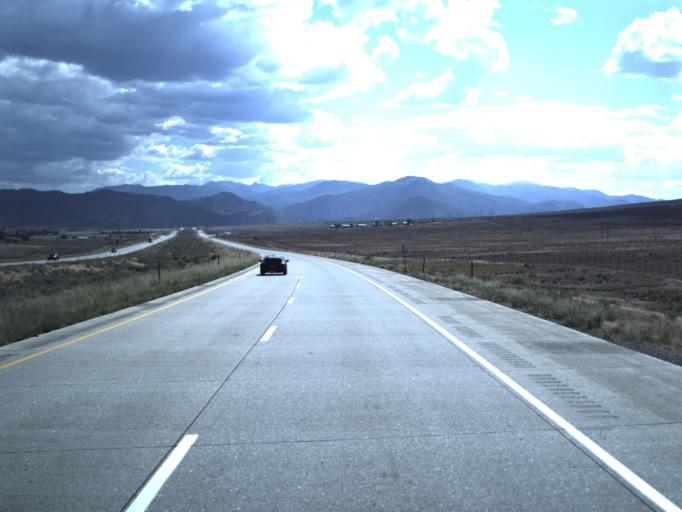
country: US
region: Utah
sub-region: Sevier County
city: Monroe
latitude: 38.6430
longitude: -112.2191
